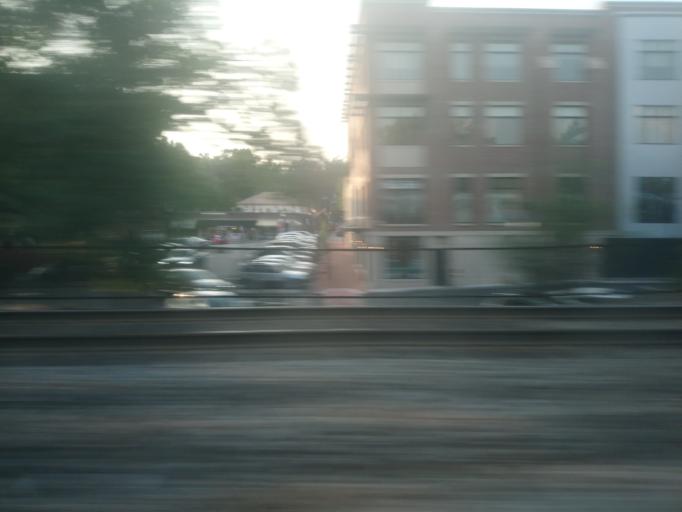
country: US
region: New Jersey
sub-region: Essex County
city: Maplewood
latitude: 40.7304
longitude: -74.2767
